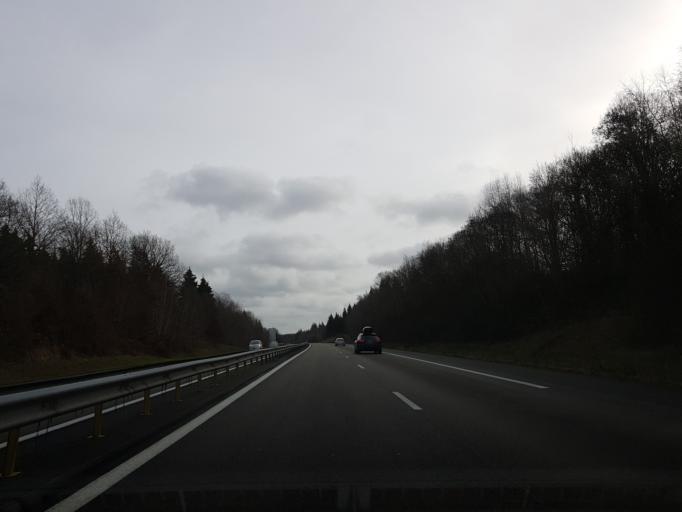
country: FR
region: Champagne-Ardenne
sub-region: Departement de l'Aube
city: Lusigny-sur-Barse
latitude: 48.1826
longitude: 4.2874
